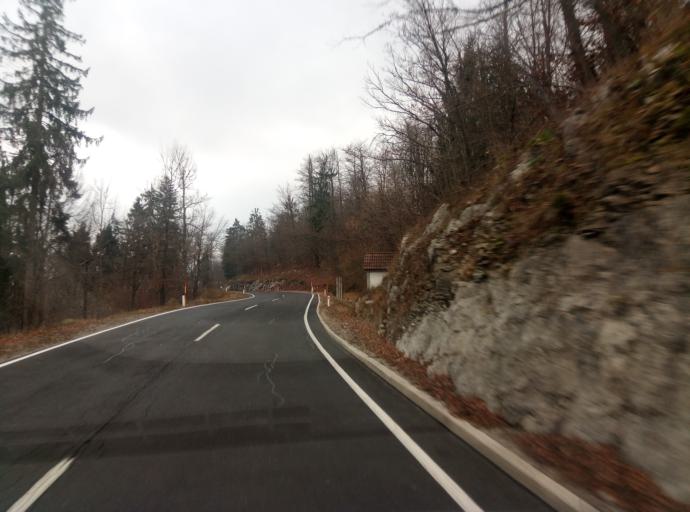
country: SI
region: Idrija
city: Idrija
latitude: 45.9489
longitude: 14.0774
